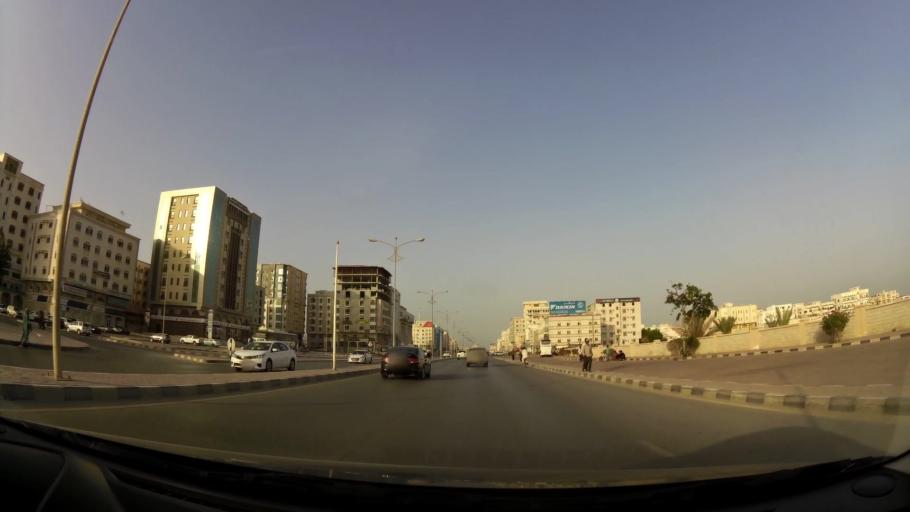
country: OM
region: Zufar
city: Salalah
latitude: 17.0161
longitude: 54.0952
